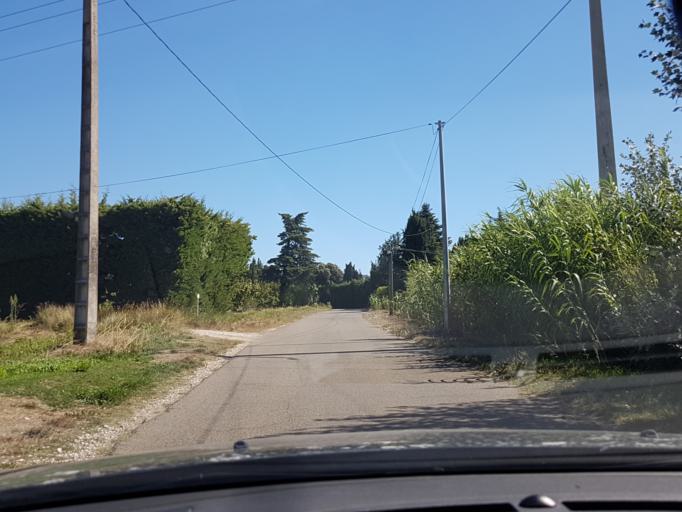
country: FR
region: Provence-Alpes-Cote d'Azur
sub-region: Departement des Bouches-du-Rhone
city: Molleges
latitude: 43.7845
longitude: 4.9228
